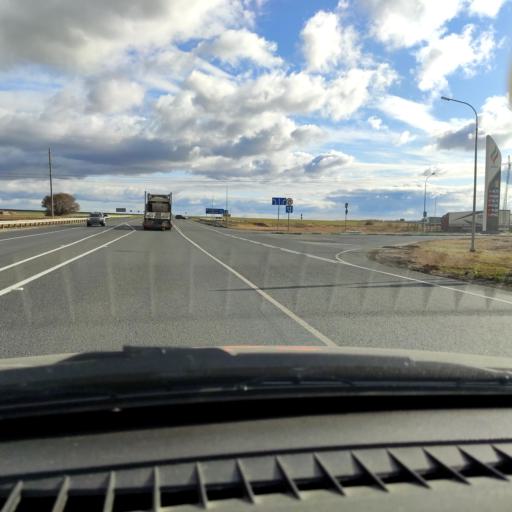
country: RU
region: Samara
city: Varlamovo
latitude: 53.2128
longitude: 48.4117
